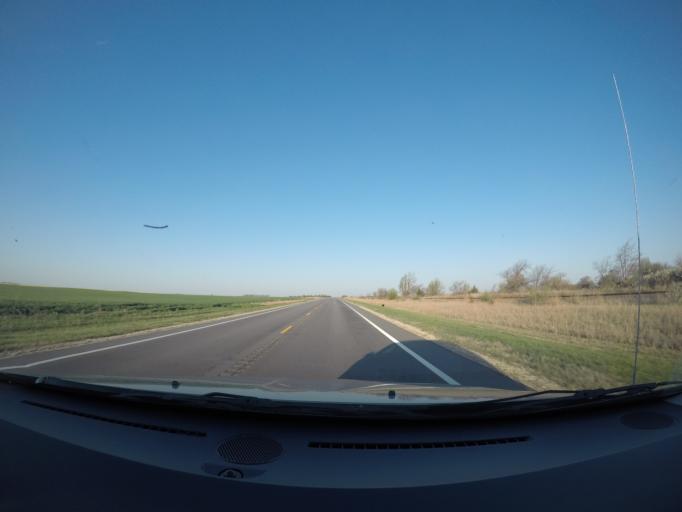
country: US
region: Kansas
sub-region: Stafford County
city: Stafford
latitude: 37.8028
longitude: -98.4500
